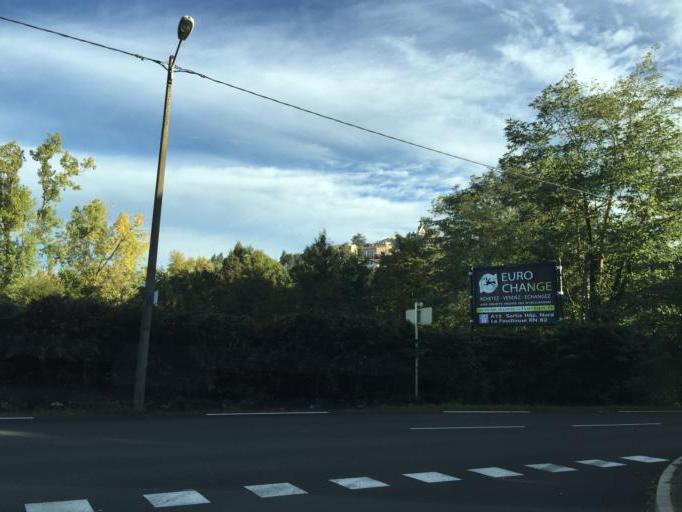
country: FR
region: Rhone-Alpes
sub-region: Departement de la Loire
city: La Tour-en-Jarez
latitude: 45.4815
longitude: 4.3871
